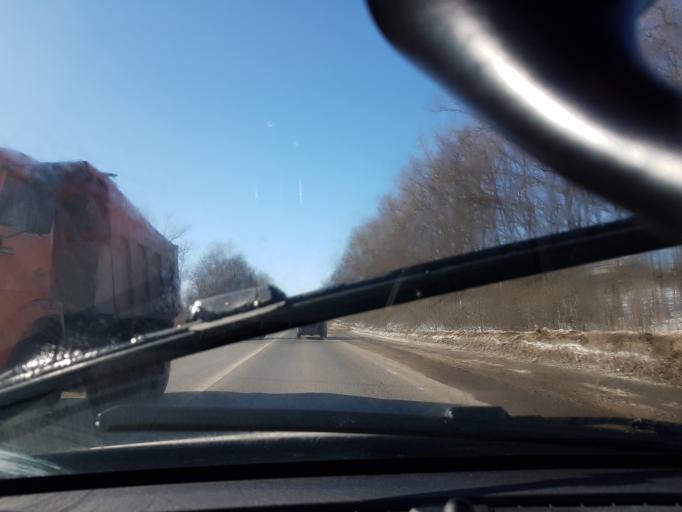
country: RU
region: Moskovskaya
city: Kostrovo
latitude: 55.9097
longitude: 36.7810
